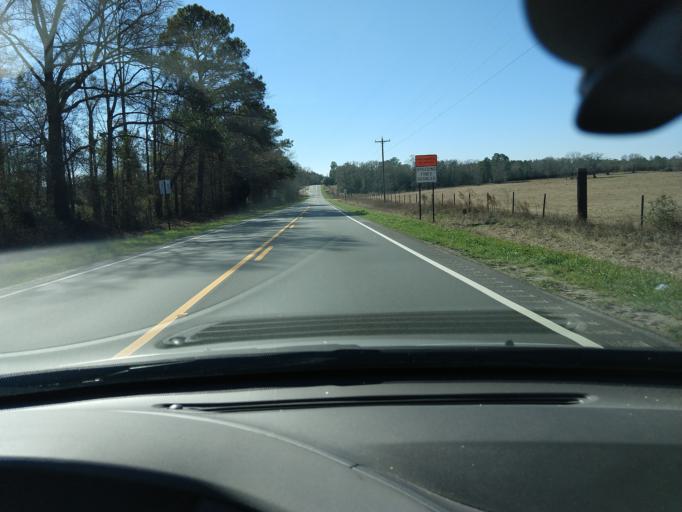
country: US
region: Alabama
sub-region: Covington County
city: Andalusia
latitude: 31.1812
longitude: -86.5771
